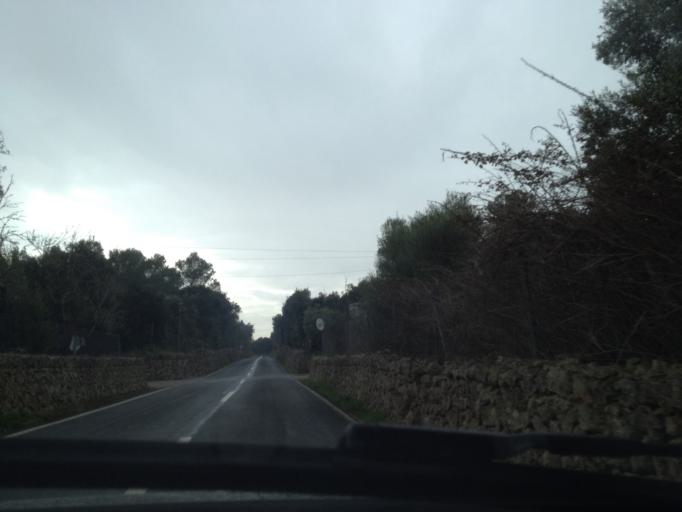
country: ES
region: Balearic Islands
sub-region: Illes Balears
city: Sineu
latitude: 39.6588
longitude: 3.0107
